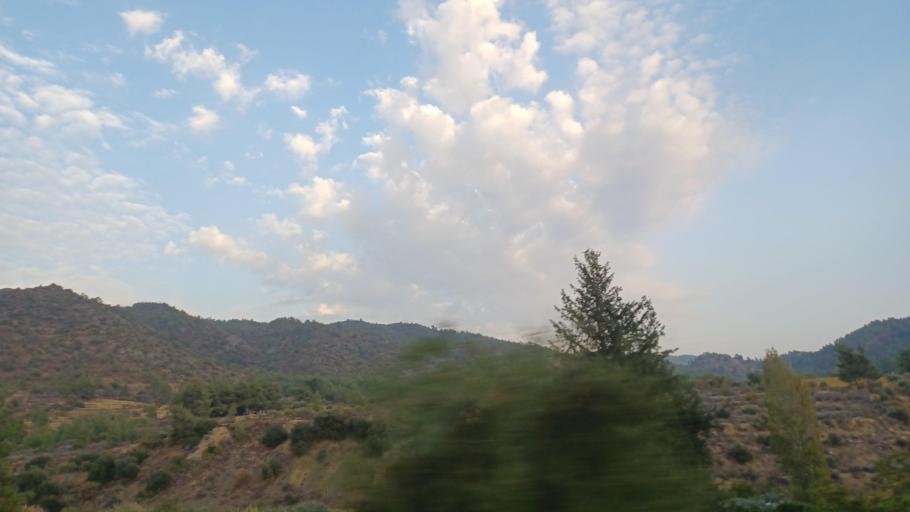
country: CY
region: Limassol
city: Pelendri
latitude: 34.8239
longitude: 32.9643
